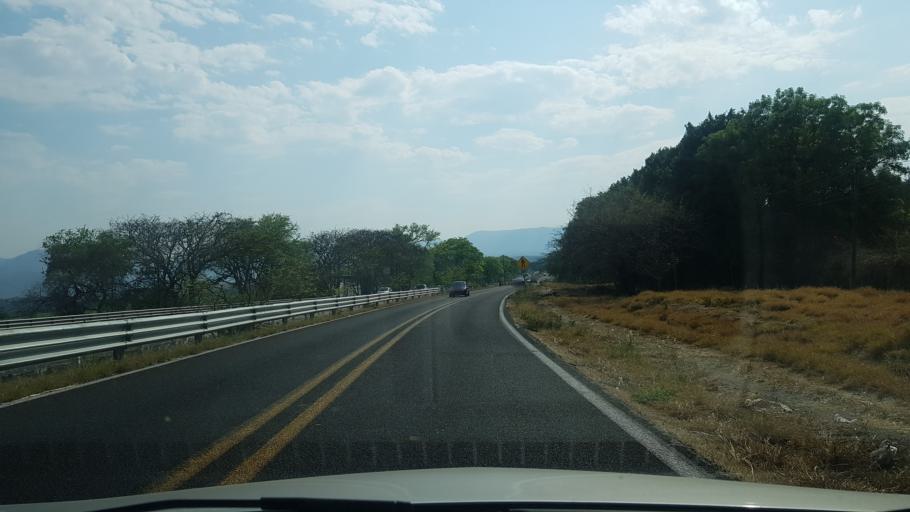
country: MX
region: Morelos
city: Puente de Ixtla
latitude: 18.6414
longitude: -99.3059
